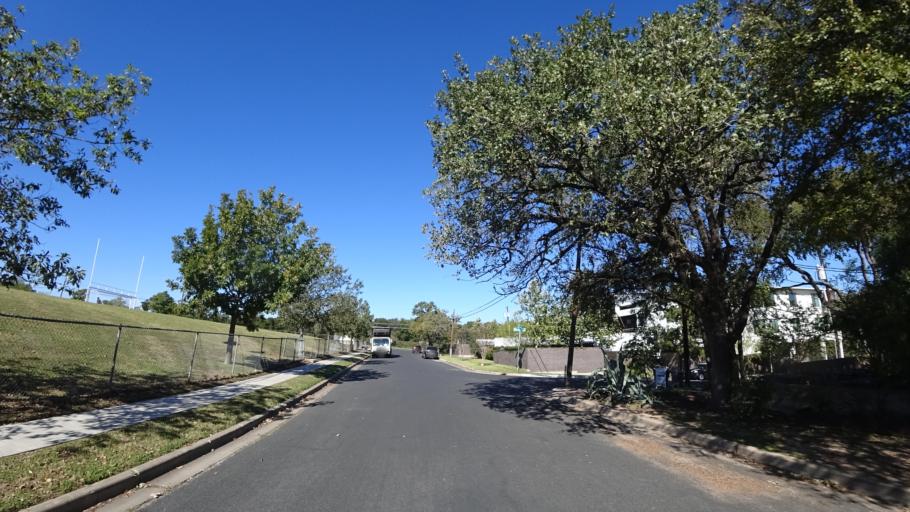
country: US
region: Texas
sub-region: Travis County
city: Rollingwood
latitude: 30.2873
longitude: -97.7730
